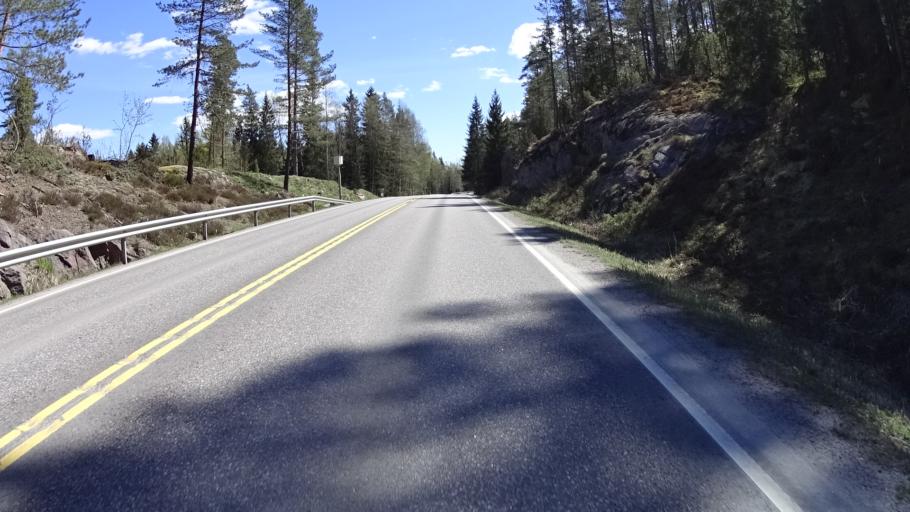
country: FI
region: Uusimaa
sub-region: Helsinki
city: Espoo
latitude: 60.3422
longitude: 24.5638
